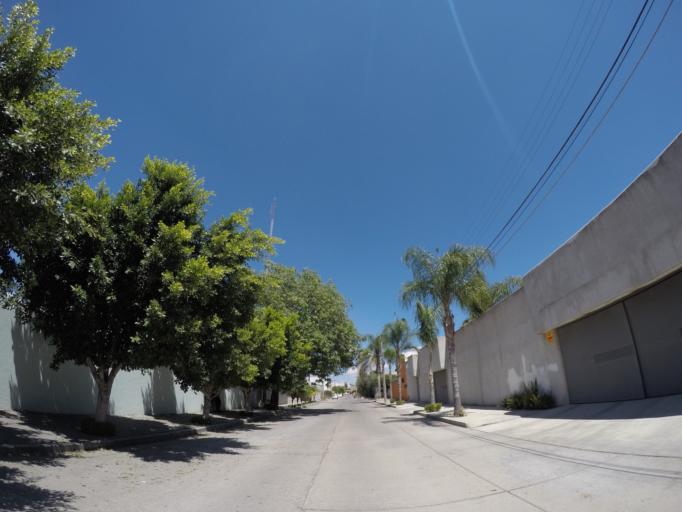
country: MX
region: San Luis Potosi
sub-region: San Luis Potosi
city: San Luis Potosi
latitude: 22.1453
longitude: -101.0120
